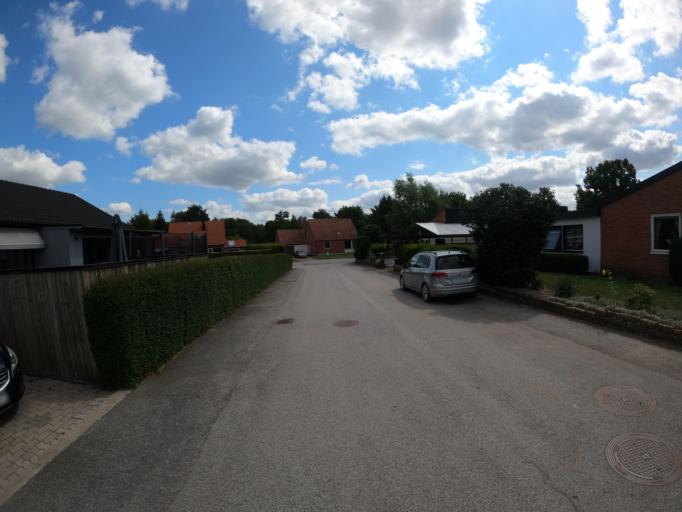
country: SE
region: Skane
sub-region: Lunds Kommun
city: Genarp
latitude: 55.5984
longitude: 13.3988
